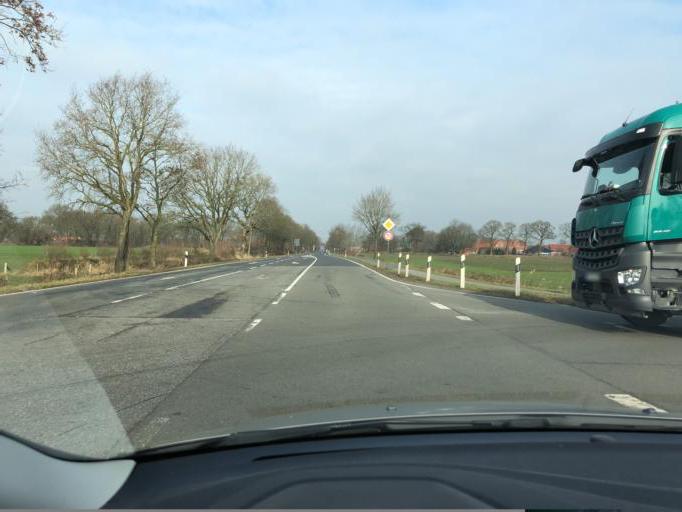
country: DE
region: Lower Saxony
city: Hesel
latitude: 53.3449
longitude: 7.6055
